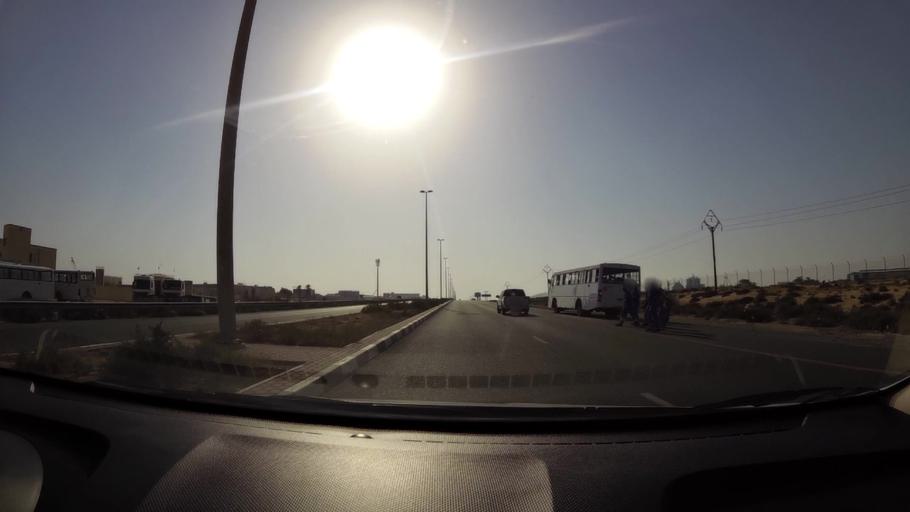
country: AE
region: Umm al Qaywayn
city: Umm al Qaywayn
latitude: 25.4366
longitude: 55.5639
